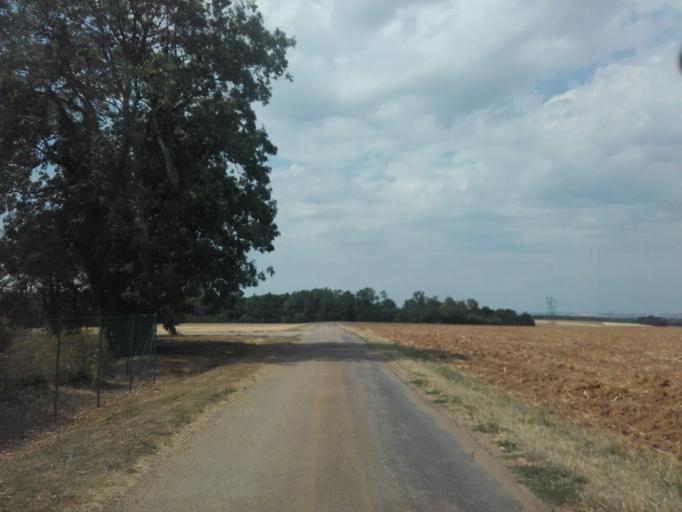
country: FR
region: Bourgogne
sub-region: Departement de l'Yonne
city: Chablis
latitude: 47.8350
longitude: 3.8462
